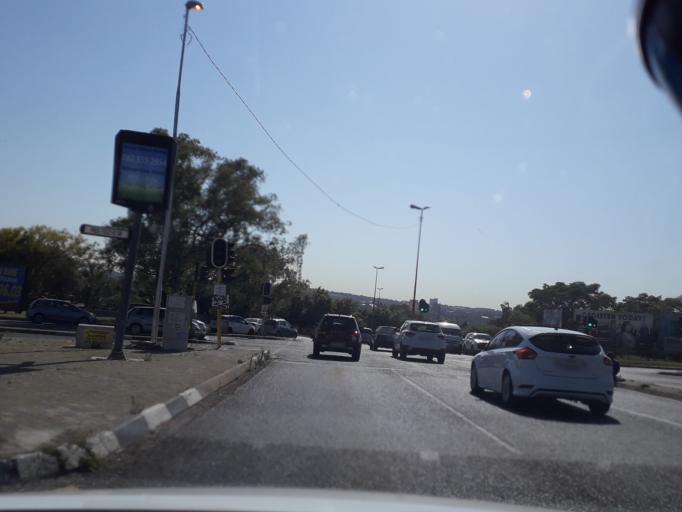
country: ZA
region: Gauteng
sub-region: City of Johannesburg Metropolitan Municipality
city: Roodepoort
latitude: -26.0918
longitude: 27.9597
